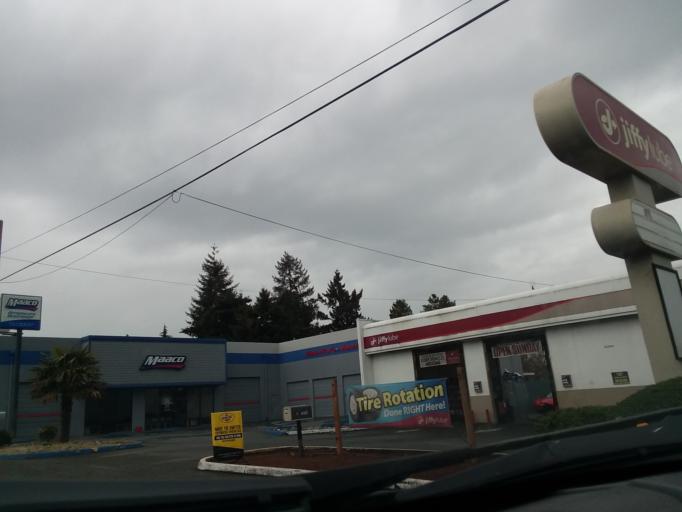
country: US
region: Washington
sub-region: King County
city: Burien
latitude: 47.4796
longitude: -122.3338
